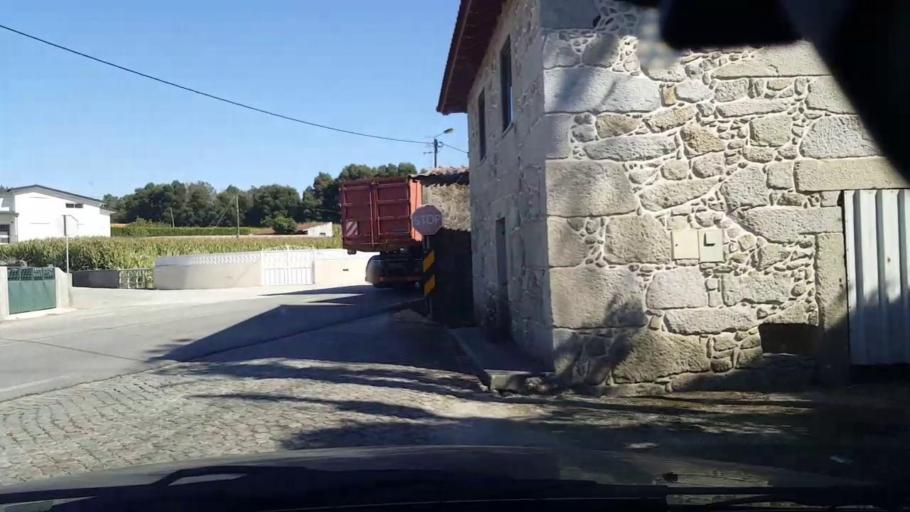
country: PT
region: Porto
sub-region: Vila do Conde
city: Arvore
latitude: 41.3333
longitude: -8.6657
